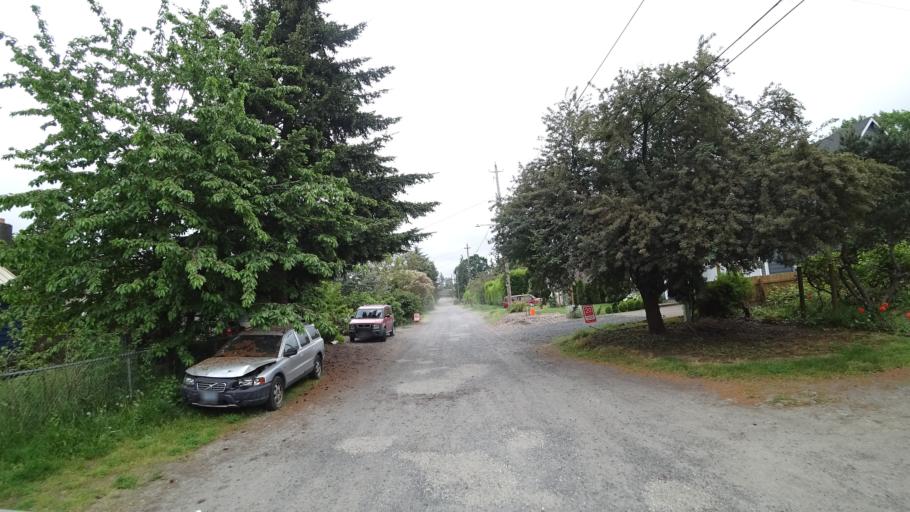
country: US
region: Oregon
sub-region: Multnomah County
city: Portland
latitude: 45.5545
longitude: -122.6053
